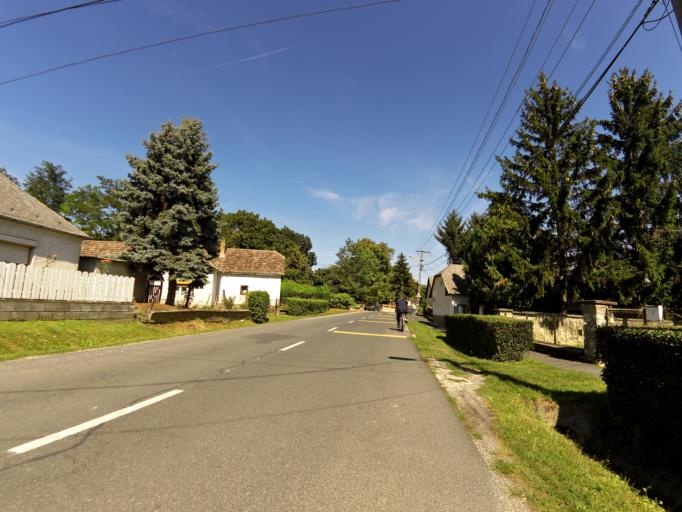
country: HU
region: Zala
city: Vonyarcvashegy
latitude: 46.8060
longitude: 17.3815
